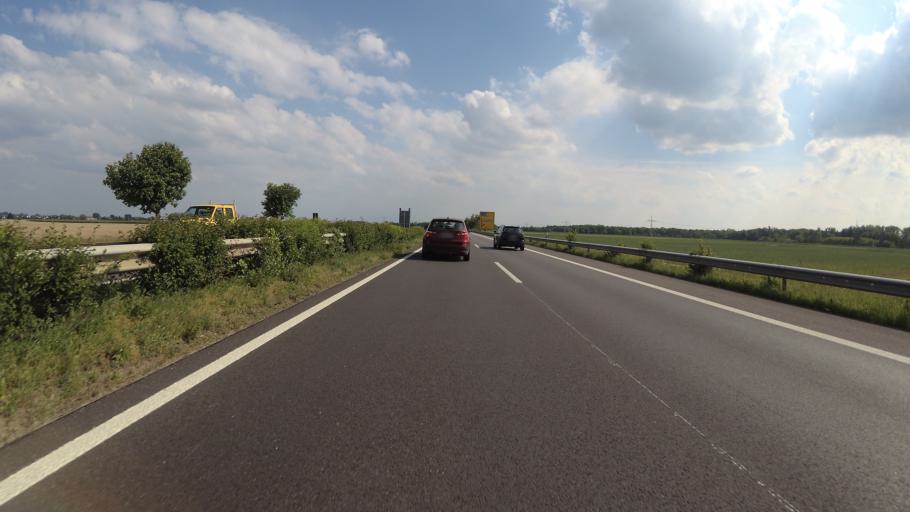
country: DE
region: Rheinland-Pfalz
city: Waldsee
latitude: 49.3974
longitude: 8.4132
